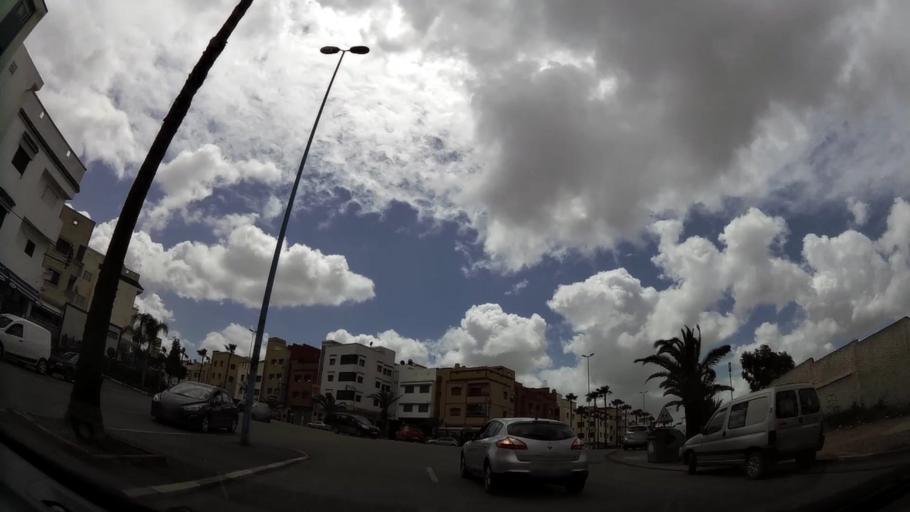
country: MA
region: Grand Casablanca
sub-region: Casablanca
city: Casablanca
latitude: 33.5399
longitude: -7.5941
